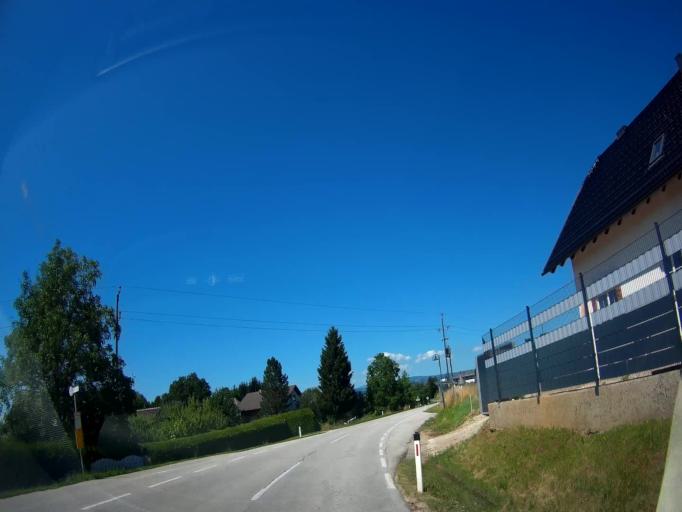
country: AT
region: Carinthia
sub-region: Politischer Bezirk Volkermarkt
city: Gallizien
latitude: 46.6047
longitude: 14.5346
